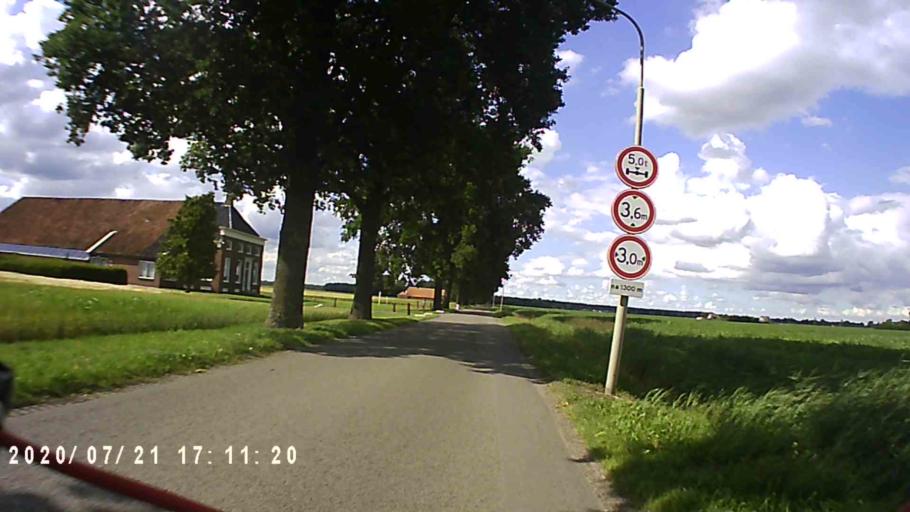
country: NL
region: Groningen
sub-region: Gemeente Hoogezand-Sappemeer
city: Hoogezand
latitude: 53.1308
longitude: 6.7590
